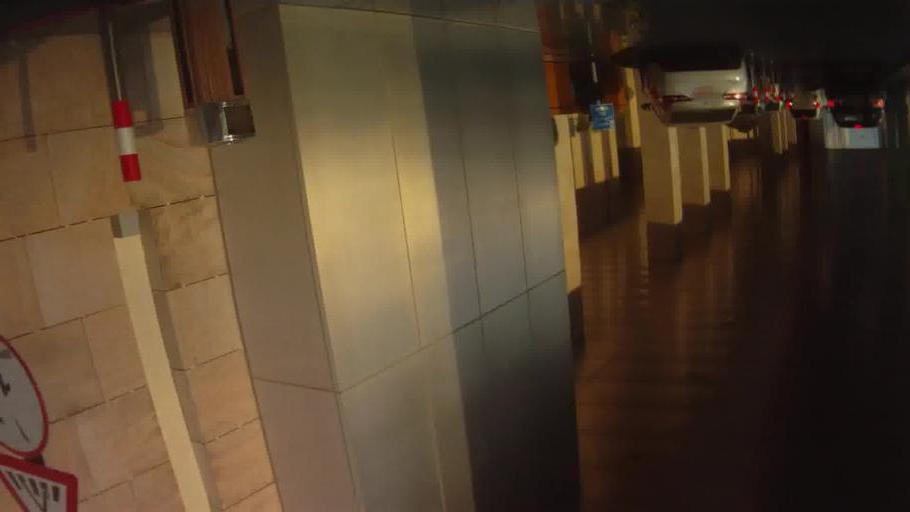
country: OM
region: Muhafazat Masqat
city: Bawshar
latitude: 23.5890
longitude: 58.4122
